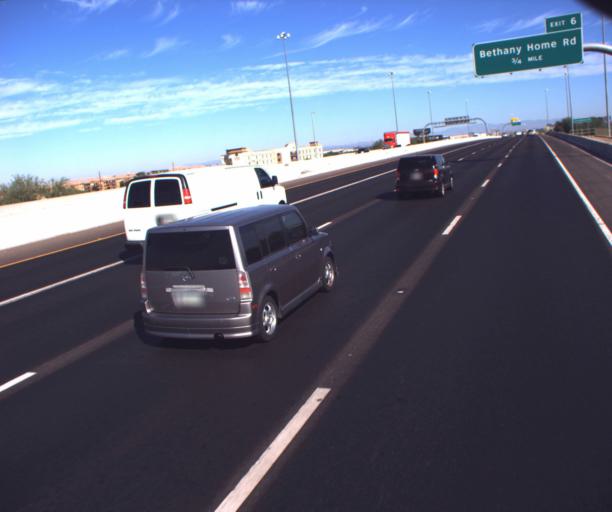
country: US
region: Arizona
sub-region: Maricopa County
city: Tolleson
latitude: 33.5070
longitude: -112.2690
